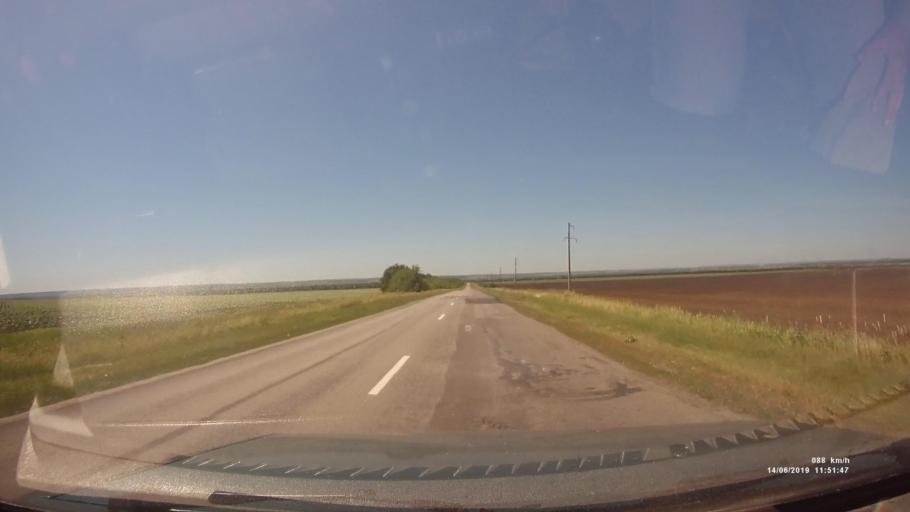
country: RU
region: Rostov
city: Kazanskaya
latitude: 49.8405
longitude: 41.2400
